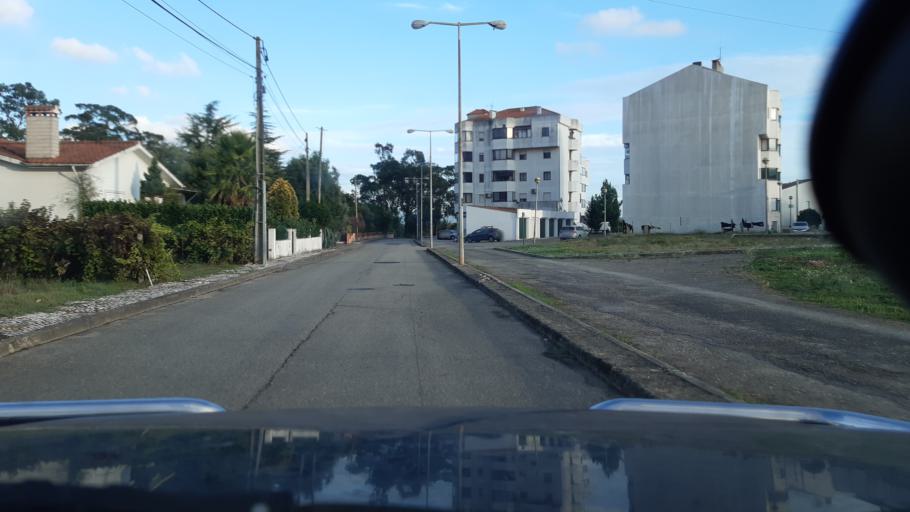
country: PT
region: Aveiro
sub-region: Agueda
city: Agueda
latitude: 40.5796
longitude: -8.4600
